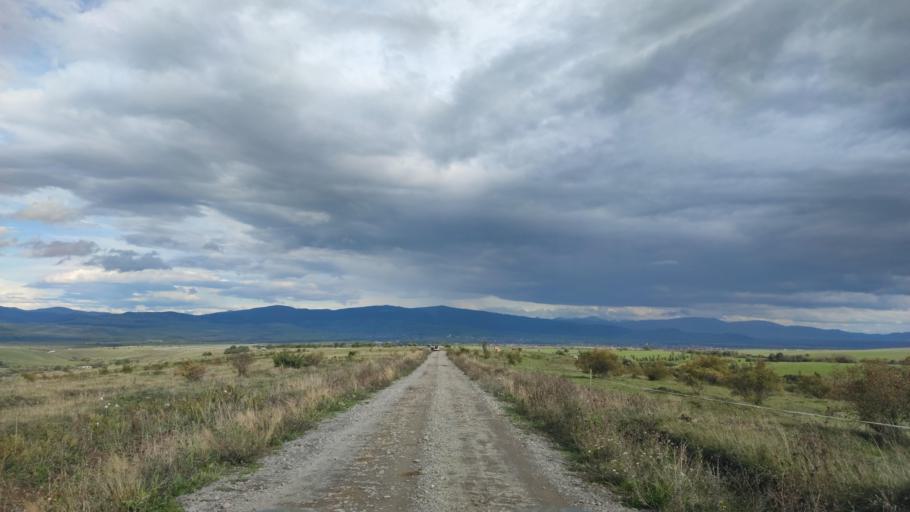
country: RO
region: Harghita
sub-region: Comuna Remetea
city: Remetea
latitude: 46.8160
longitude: 25.3759
